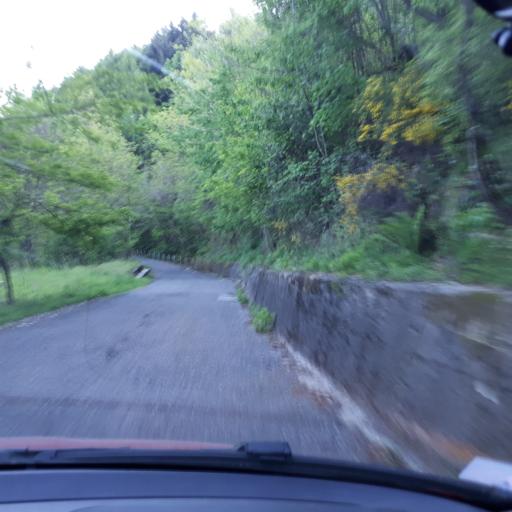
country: IT
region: Lombardy
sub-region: Provincia di Como
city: Musso
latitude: 46.1144
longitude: 9.2681
